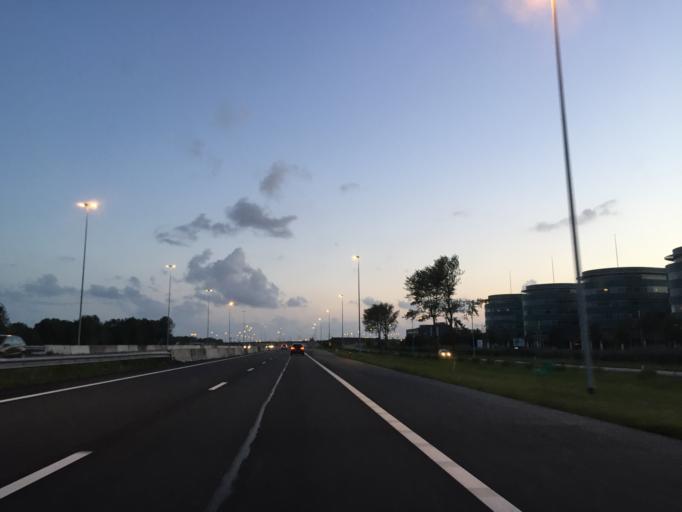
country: NL
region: Flevoland
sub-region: Gemeente Almere
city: Almere Stad
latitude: 52.3466
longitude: 5.1857
